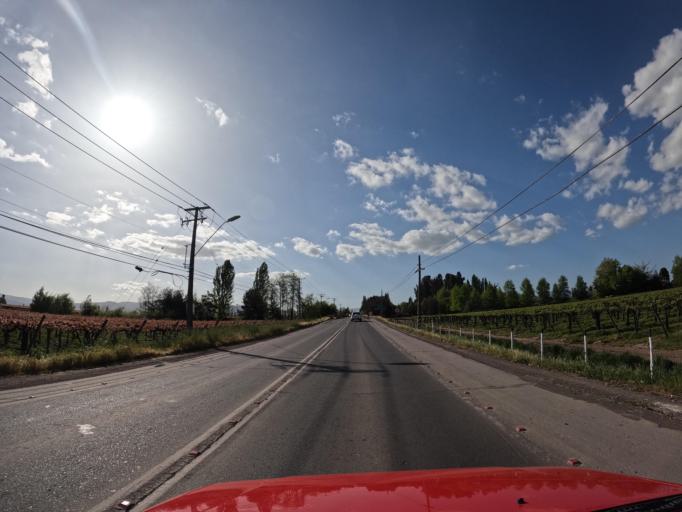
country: CL
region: Maule
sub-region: Provincia de Curico
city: Curico
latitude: -34.9564
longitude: -71.2535
